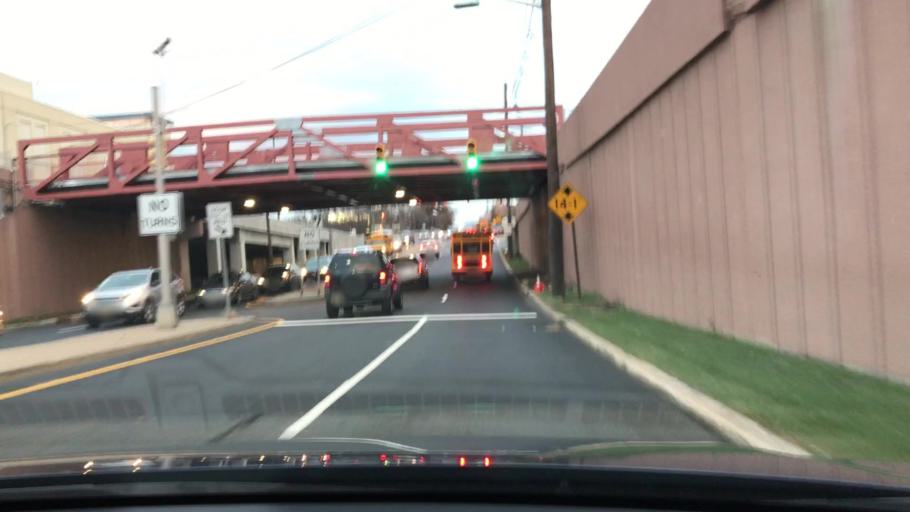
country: US
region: New Jersey
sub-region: Bergen County
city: Maywood
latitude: 40.9136
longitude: -74.0565
